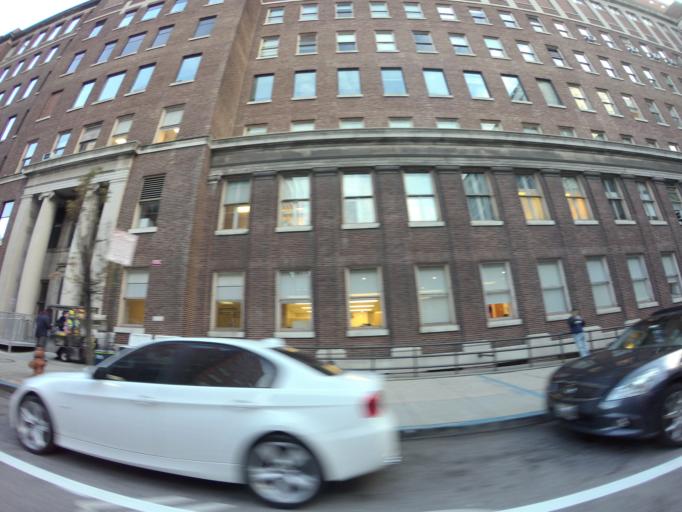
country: US
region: Maryland
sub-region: City of Baltimore
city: Baltimore
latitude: 39.2985
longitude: -76.5916
